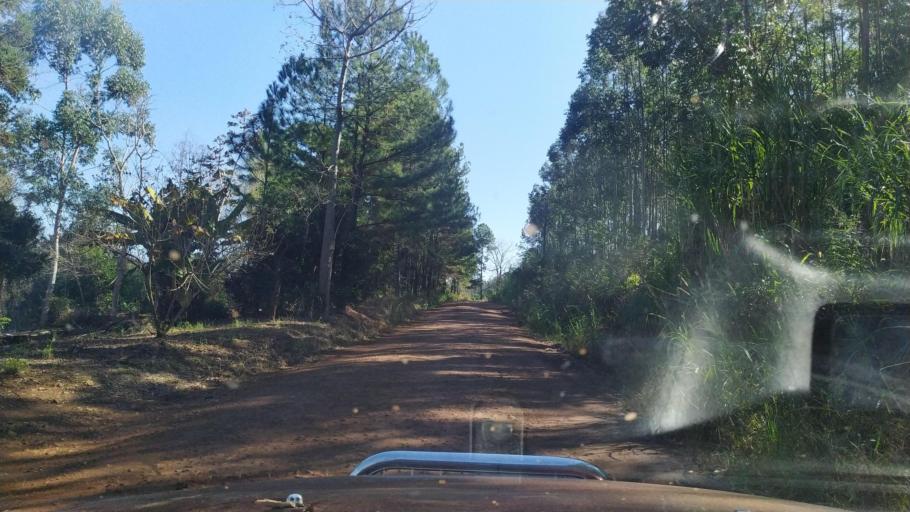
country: AR
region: Misiones
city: El Alcazar
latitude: -26.7238
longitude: -54.6843
